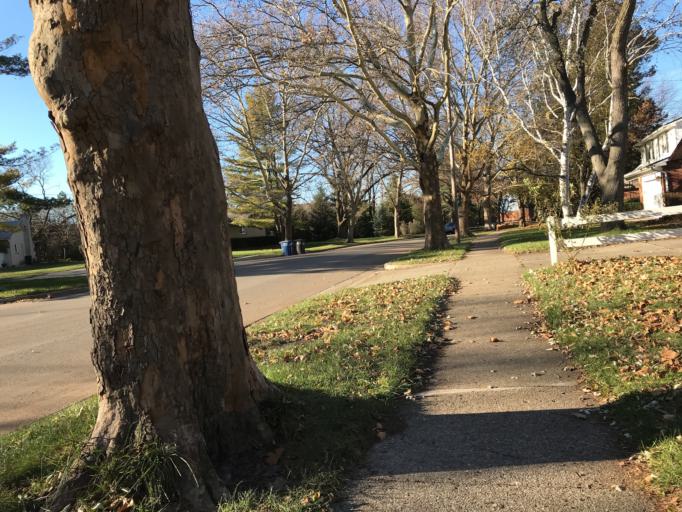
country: US
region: Michigan
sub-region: Washtenaw County
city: Ann Arbor
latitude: 42.2495
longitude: -83.7285
